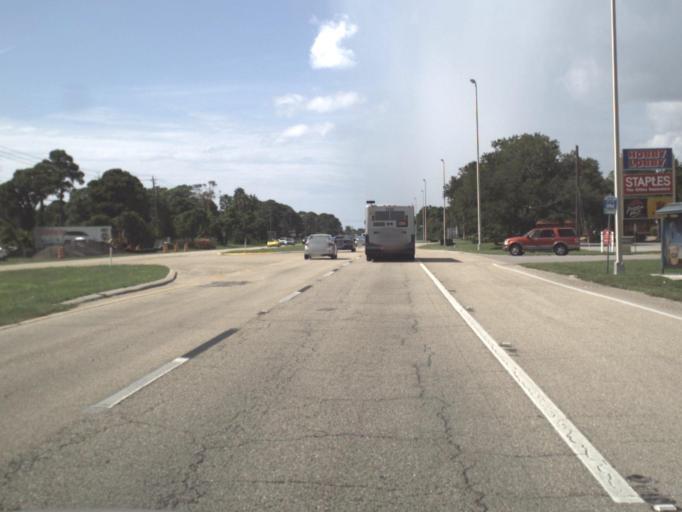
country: US
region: Florida
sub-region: Sarasota County
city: Vamo
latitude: 27.2348
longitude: -82.4991
